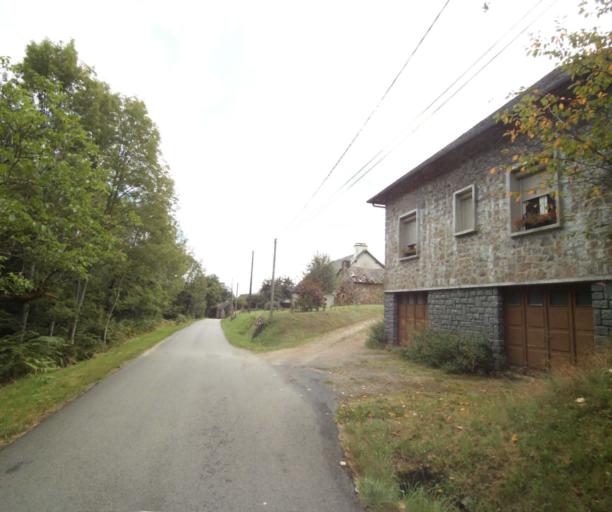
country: FR
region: Limousin
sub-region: Departement de la Correze
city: Sainte-Fortunade
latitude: 45.1973
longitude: 1.8238
